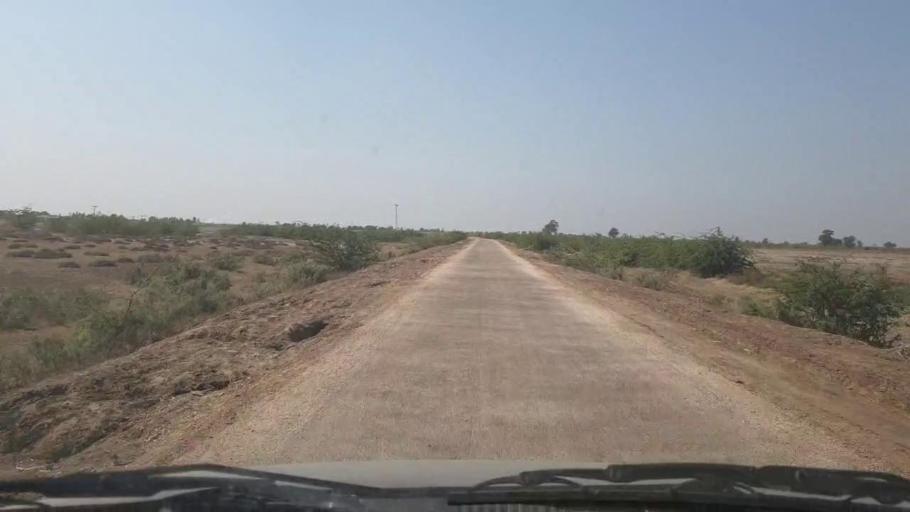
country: PK
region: Sindh
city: Samaro
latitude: 25.2580
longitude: 69.3278
